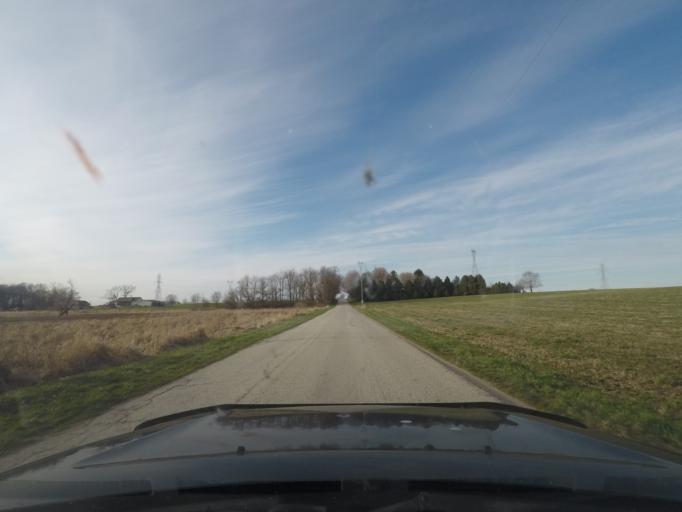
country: US
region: Indiana
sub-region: LaPorte County
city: LaPorte
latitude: 41.5440
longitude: -86.7987
